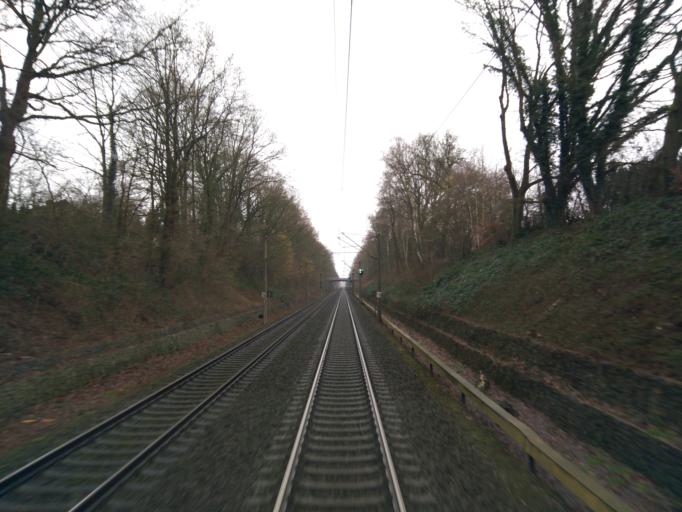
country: DE
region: Lower Saxony
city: Buchholz in der Nordheide
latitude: 53.3288
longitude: 9.8866
